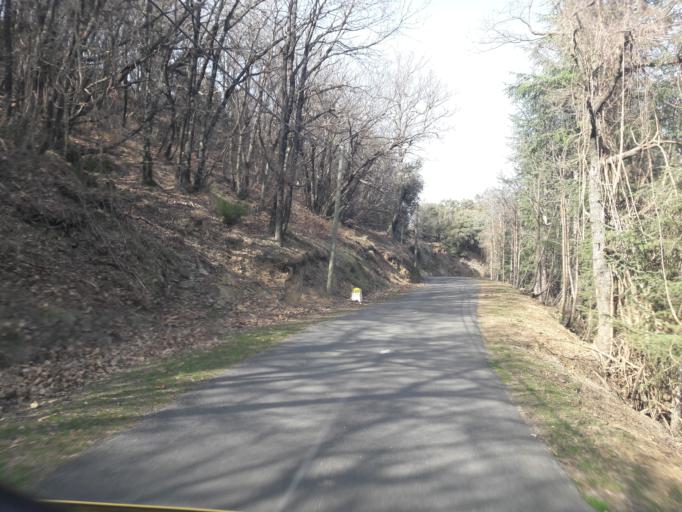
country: FR
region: Languedoc-Roussillon
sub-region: Departement du Gard
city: Sumene
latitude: 44.0084
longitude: 3.7777
